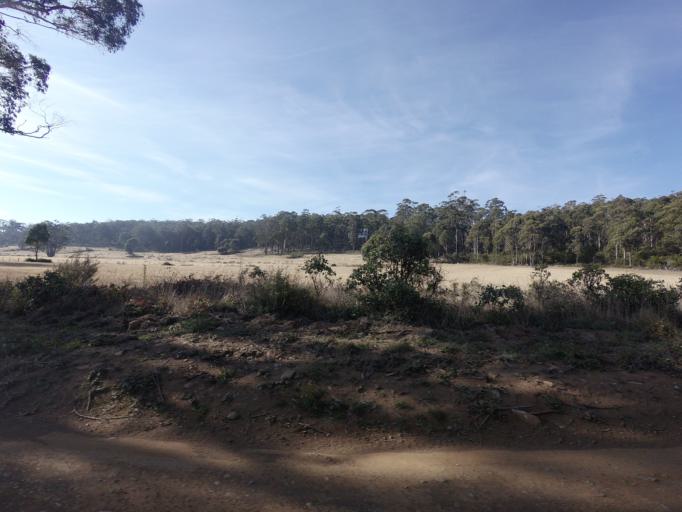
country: AU
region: Tasmania
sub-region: Sorell
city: Sorell
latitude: -42.4802
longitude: 147.4843
